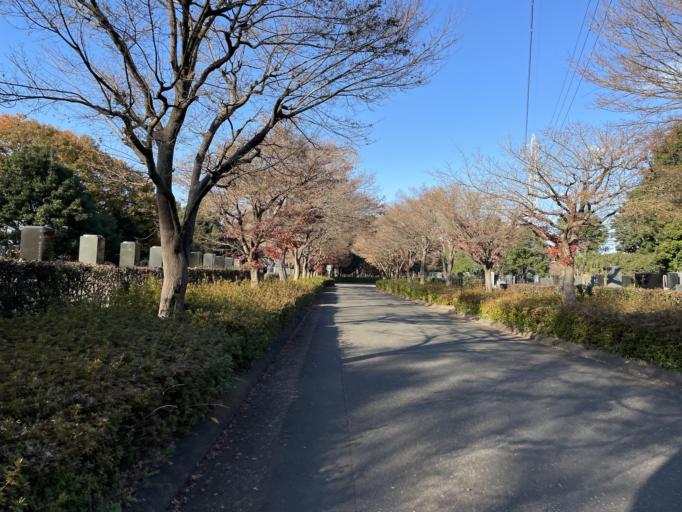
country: JP
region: Saitama
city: Asaka
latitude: 35.7795
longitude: 139.5788
